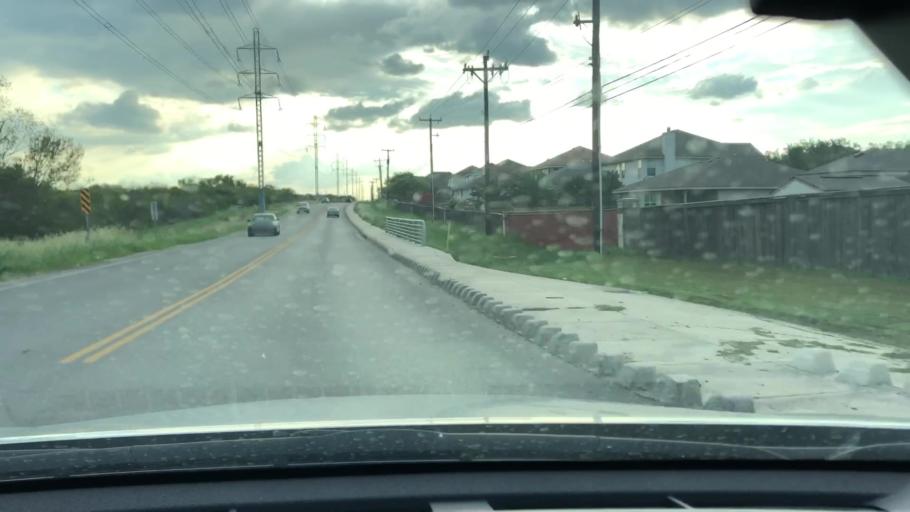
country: US
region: Texas
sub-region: Bexar County
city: Kirby
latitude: 29.4662
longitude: -98.3453
